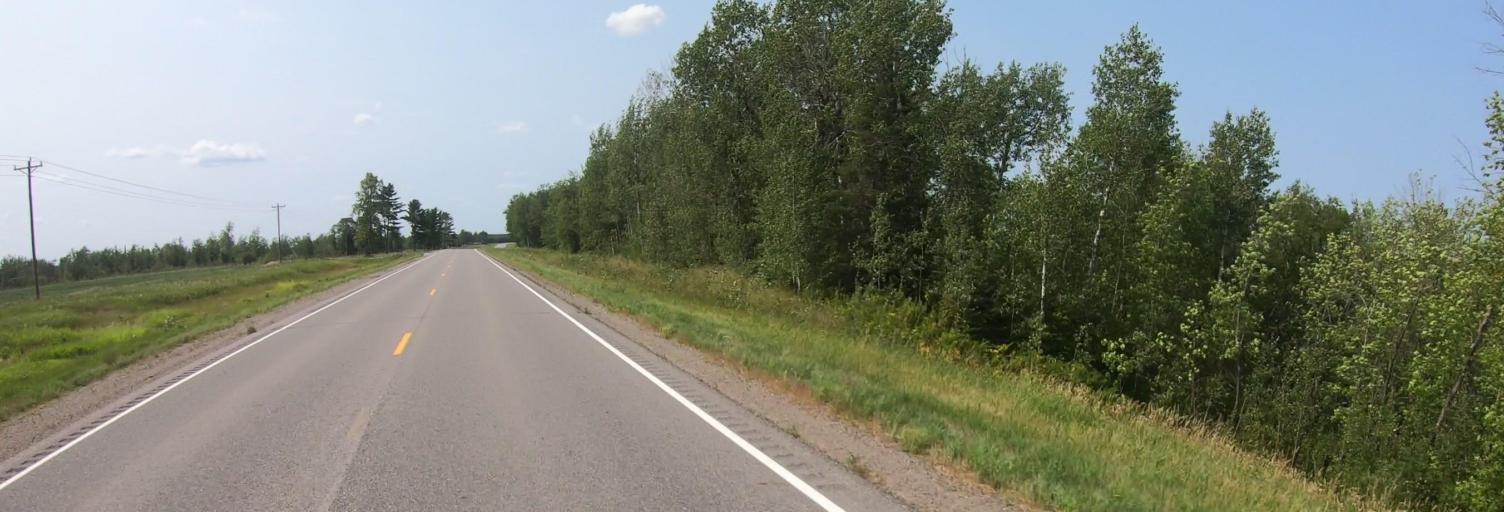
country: US
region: Minnesota
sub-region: Lake of the Woods County
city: Baudette
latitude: 48.6478
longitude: -94.2107
